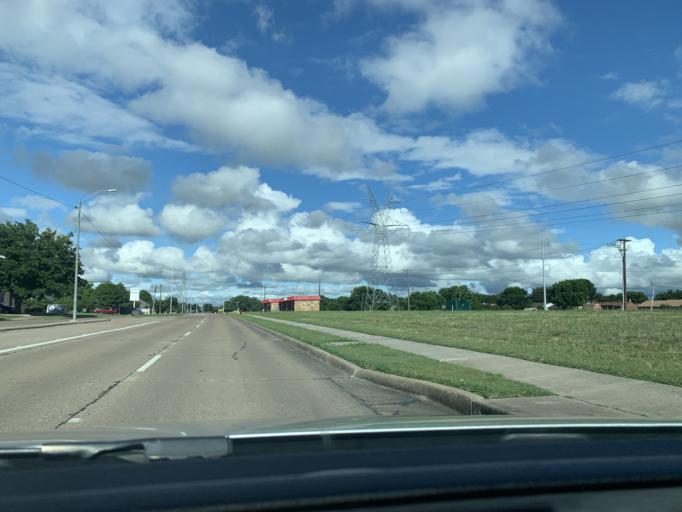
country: US
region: Texas
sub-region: Dallas County
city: Grand Prairie
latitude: 32.6583
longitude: -97.0266
